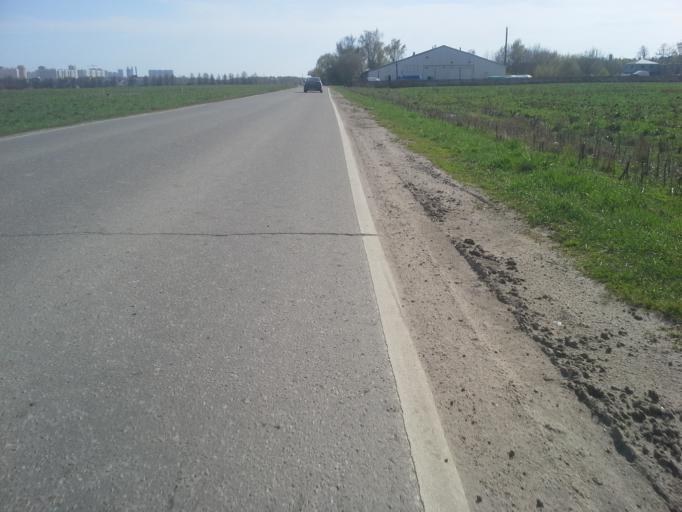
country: RU
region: Moskovskaya
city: Dubrovitsy
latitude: 55.4468
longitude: 37.4779
